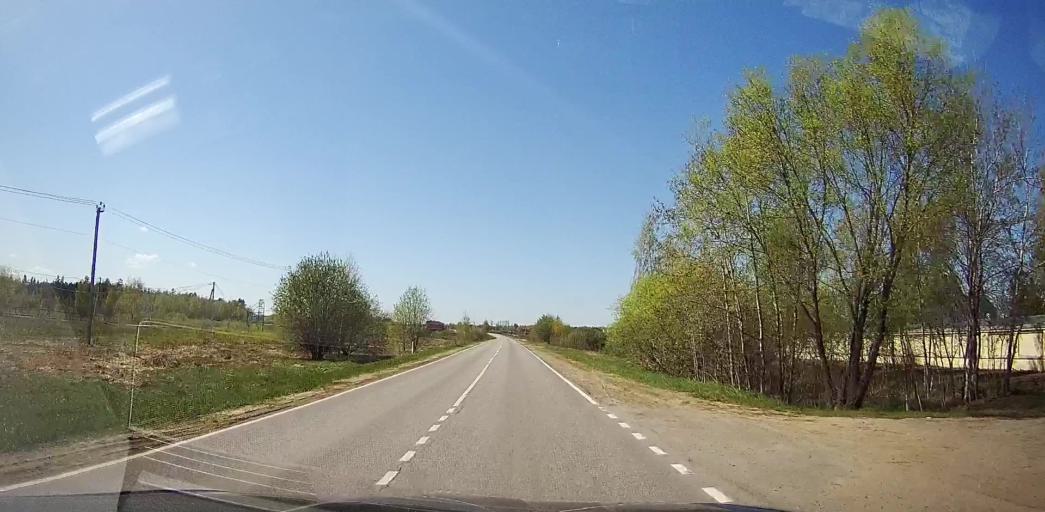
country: RU
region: Moskovskaya
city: Bronnitsy
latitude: 55.4564
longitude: 38.2903
